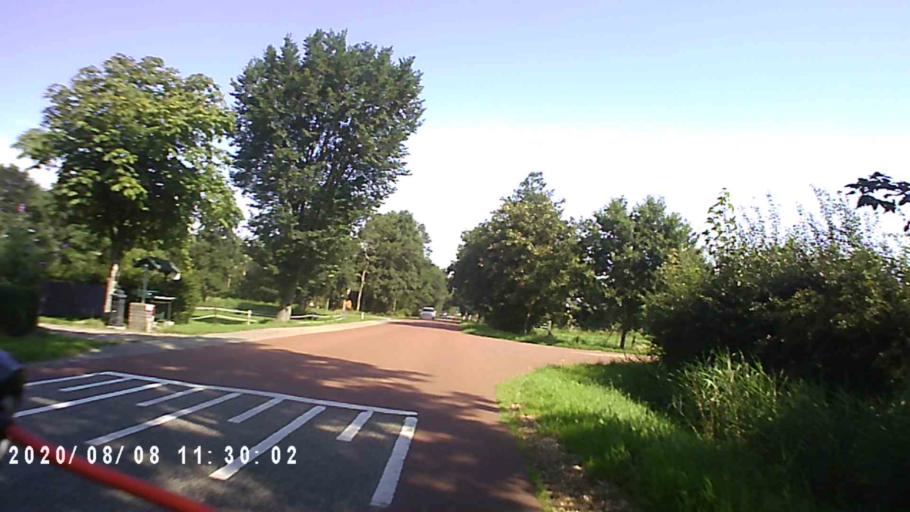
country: NL
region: Groningen
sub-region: Gemeente Leek
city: Leek
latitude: 53.1988
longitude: 6.3870
